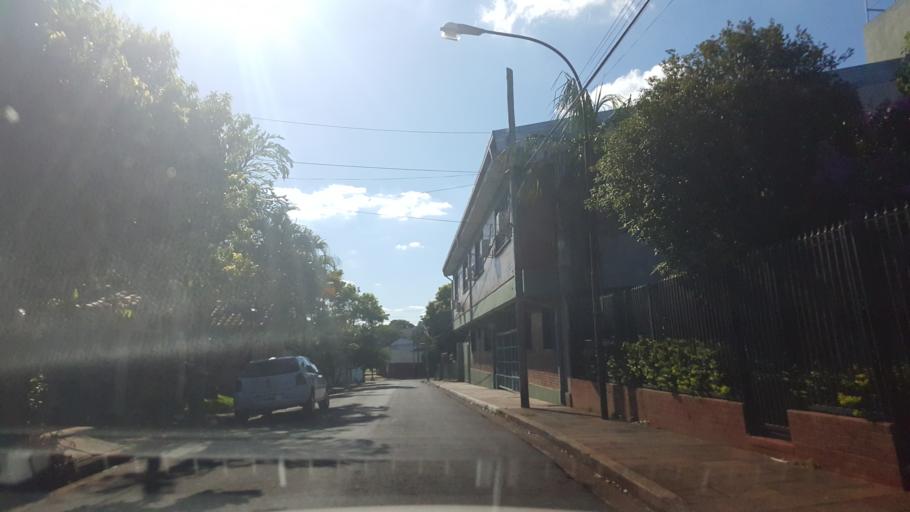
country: AR
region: Misiones
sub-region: Departamento de Capital
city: Posadas
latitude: -27.3928
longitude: -55.8965
